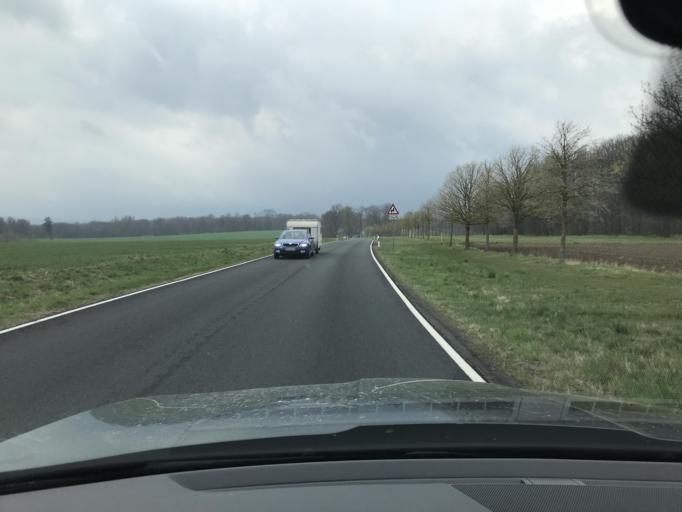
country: DE
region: Saxony-Anhalt
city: Harzgerode
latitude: 51.6539
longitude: 11.1369
